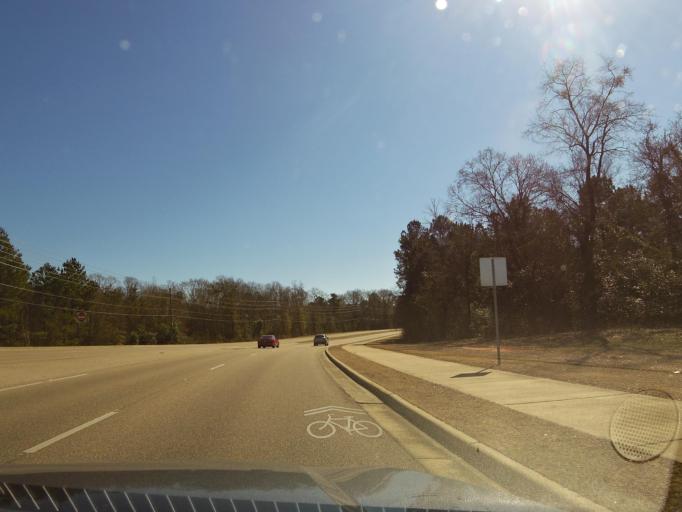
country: US
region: Alabama
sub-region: Elmore County
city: Millbrook
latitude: 32.4777
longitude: -86.4049
